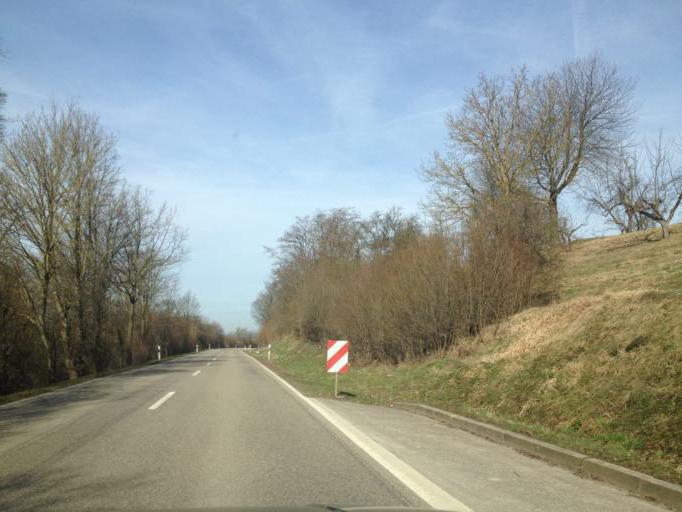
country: DE
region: Baden-Wuerttemberg
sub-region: Regierungsbezirk Stuttgart
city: Oedheim
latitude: 49.2203
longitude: 9.2729
